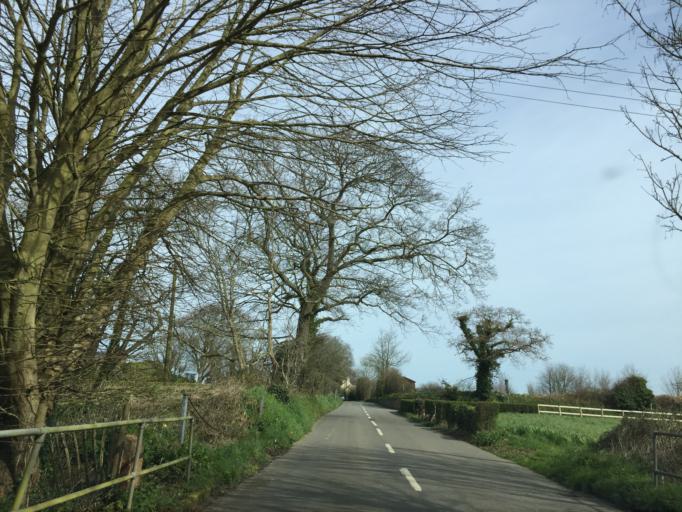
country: JE
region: St Helier
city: Saint Helier
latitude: 49.2252
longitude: -2.0586
